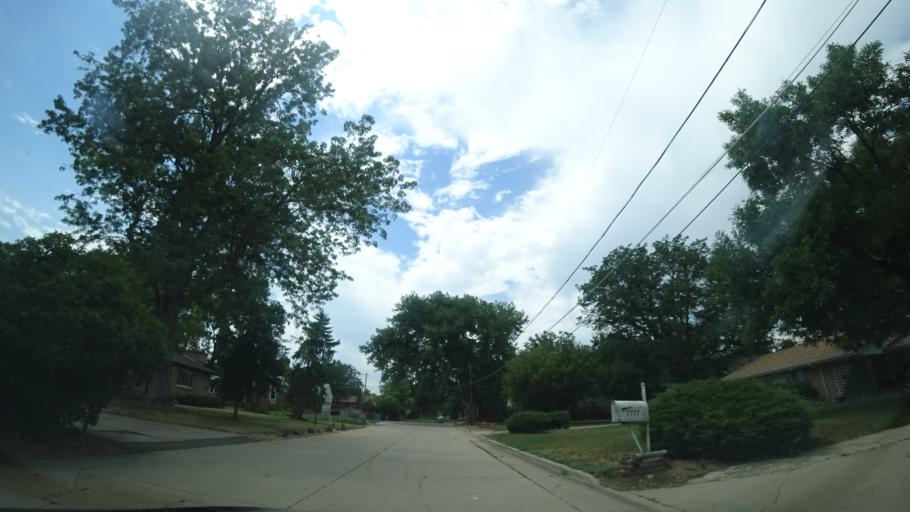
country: US
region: Colorado
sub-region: Jefferson County
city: Lakewood
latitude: 39.7203
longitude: -105.0831
